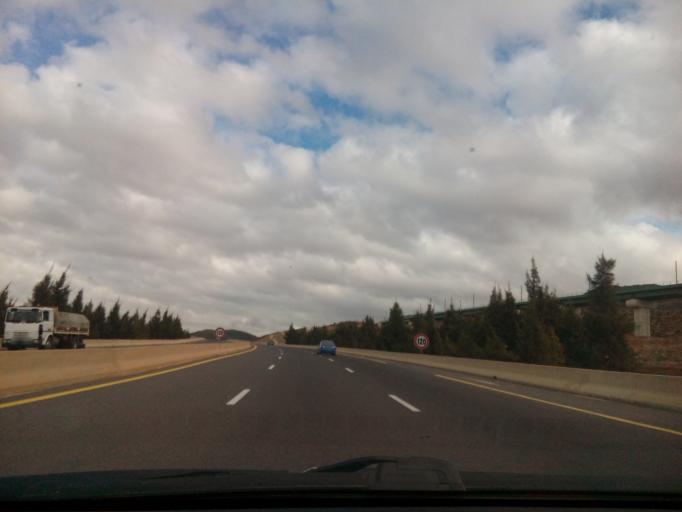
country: DZ
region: Tlemcen
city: Sidi Abdelli
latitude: 35.0103
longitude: -1.1612
